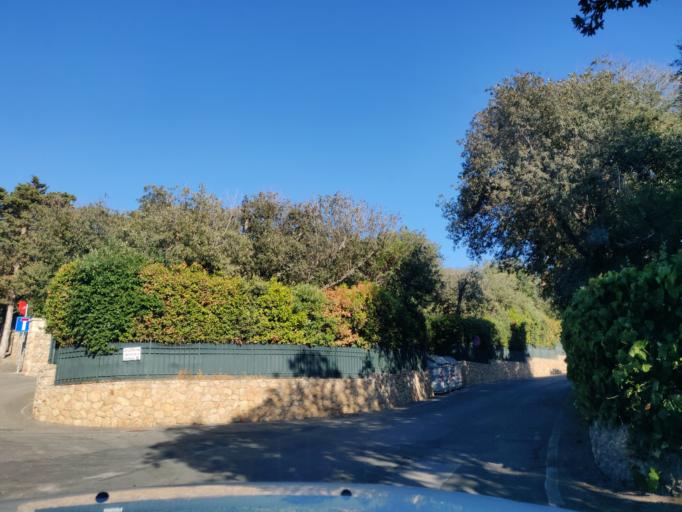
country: IT
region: Tuscany
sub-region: Provincia di Grosseto
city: Orbetello Scalo
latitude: 42.4088
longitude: 11.2828
